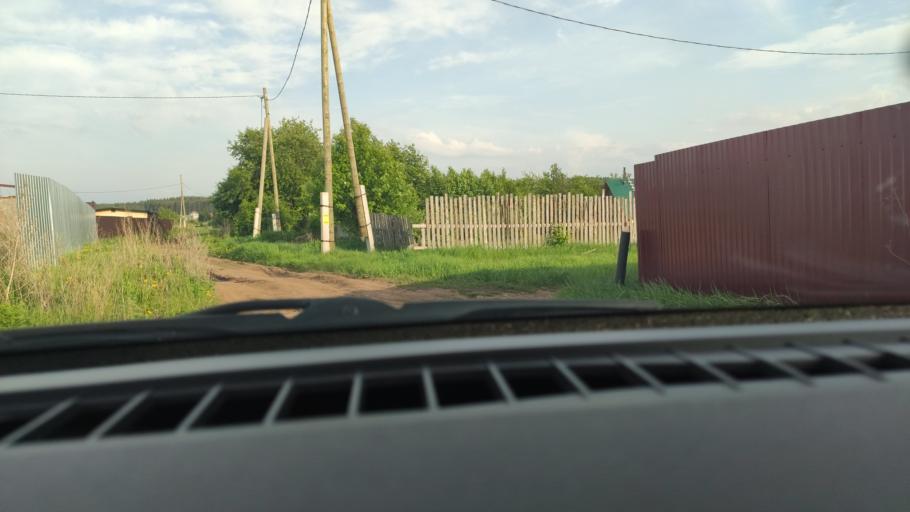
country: RU
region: Perm
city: Kultayevo
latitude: 57.8977
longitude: 55.9977
